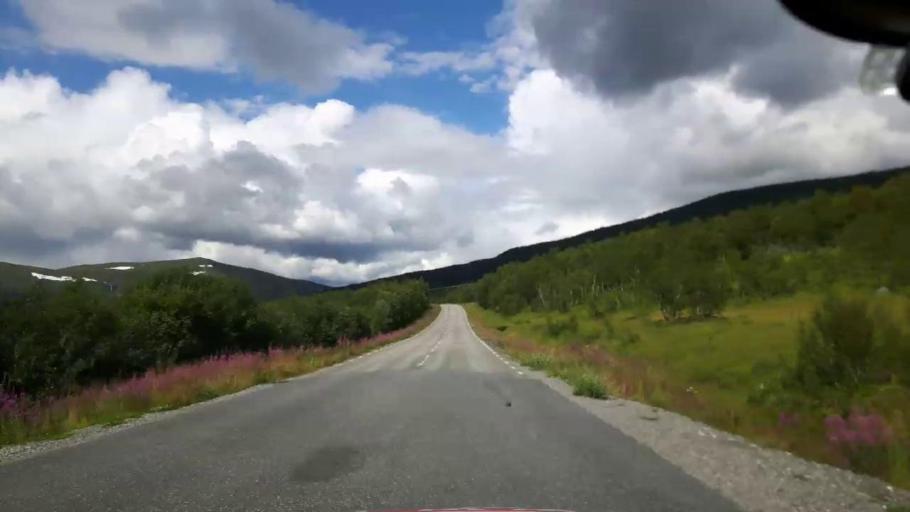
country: NO
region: Nordland
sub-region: Hattfjelldal
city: Hattfjelldal
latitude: 65.0583
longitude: 14.7189
